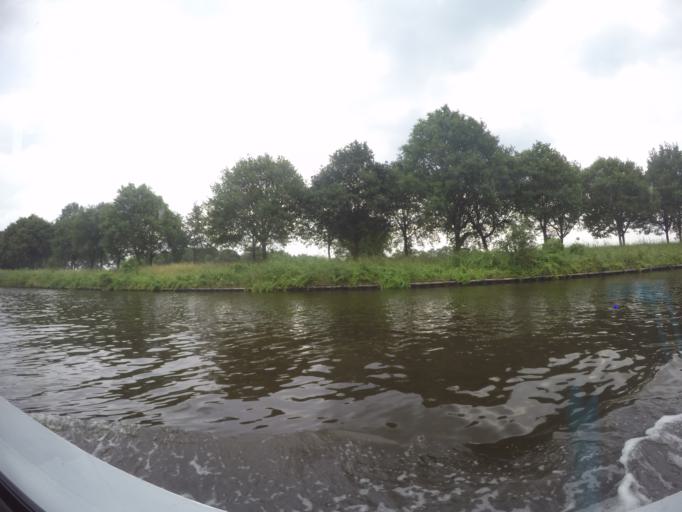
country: NL
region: Overijssel
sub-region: Gemeente Hof van Twente
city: Delden
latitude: 52.2717
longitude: 6.6439
